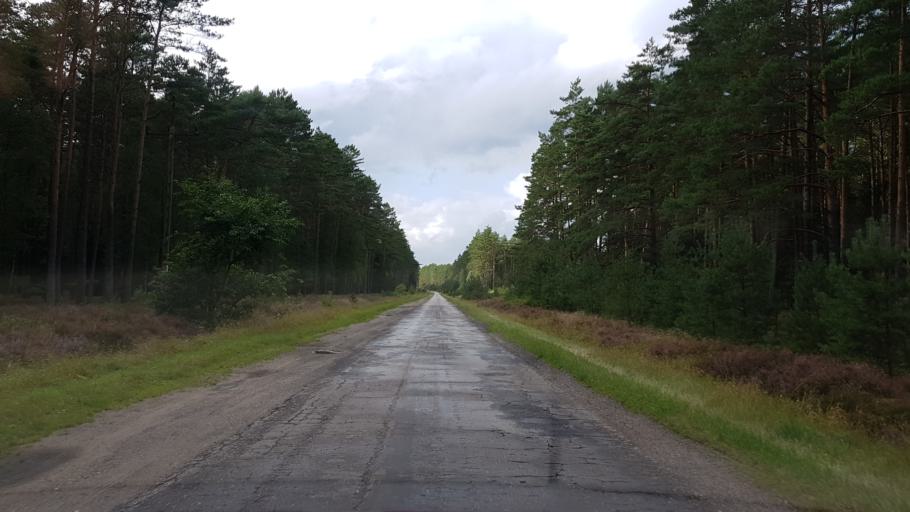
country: PL
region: West Pomeranian Voivodeship
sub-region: Powiat bialogardzki
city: Tychowo
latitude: 54.0371
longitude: 16.3351
